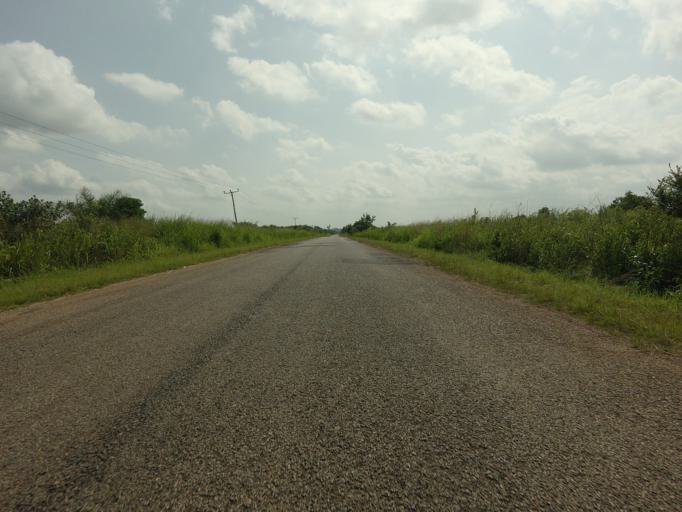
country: TG
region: Maritime
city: Tsevie
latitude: 6.3923
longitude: 0.8239
